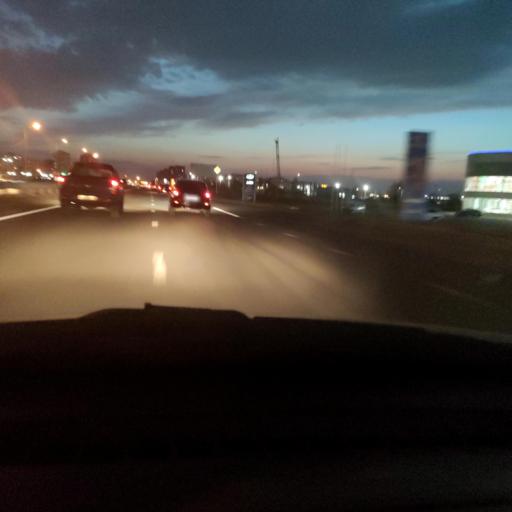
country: RU
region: Samara
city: Tol'yatti
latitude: 53.5533
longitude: 49.3410
